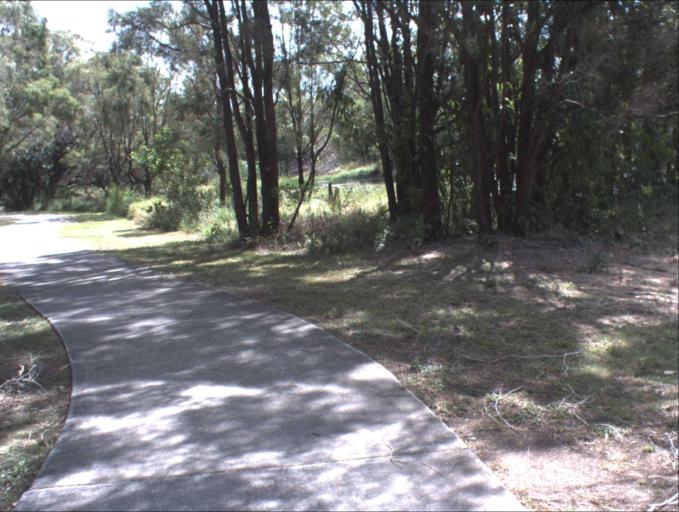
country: AU
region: Queensland
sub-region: Logan
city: Slacks Creek
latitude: -27.6713
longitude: 153.1558
